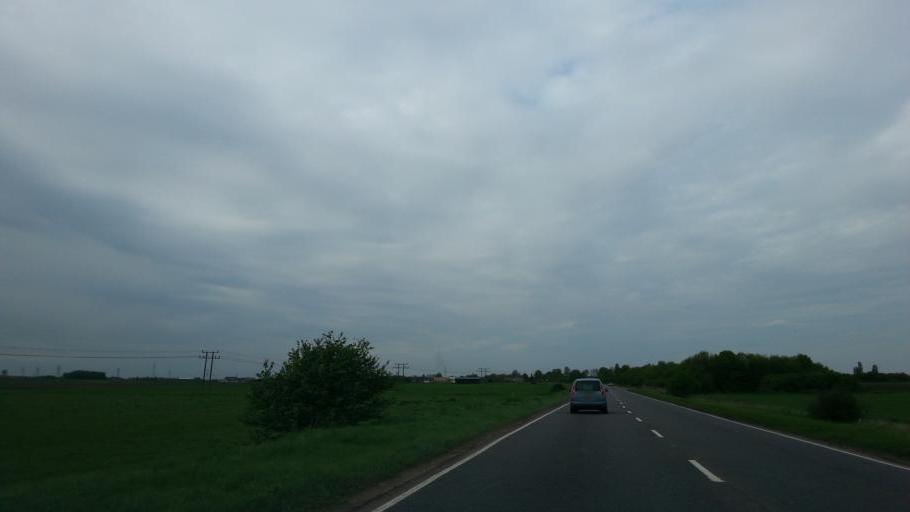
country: GB
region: England
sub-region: Cambridgeshire
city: March
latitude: 52.5374
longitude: 0.0696
